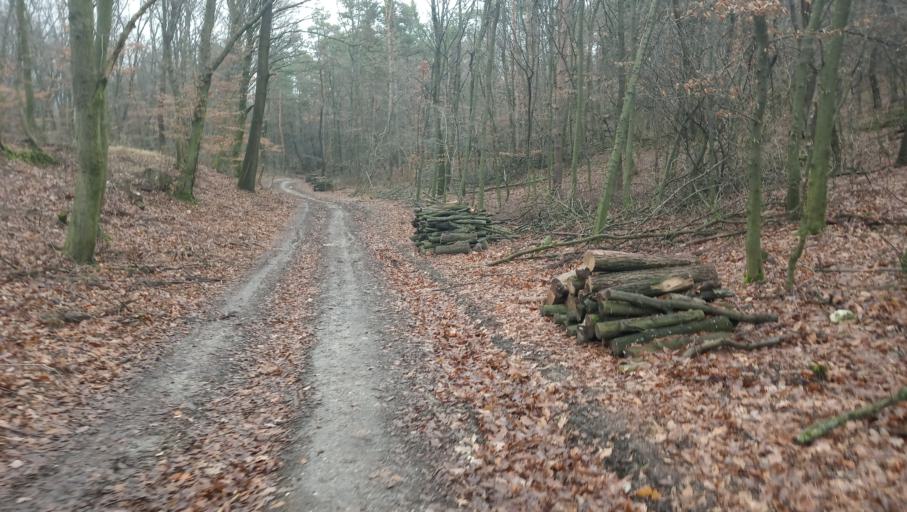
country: HU
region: Komarom-Esztergom
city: Piliscsev
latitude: 47.6681
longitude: 18.8326
